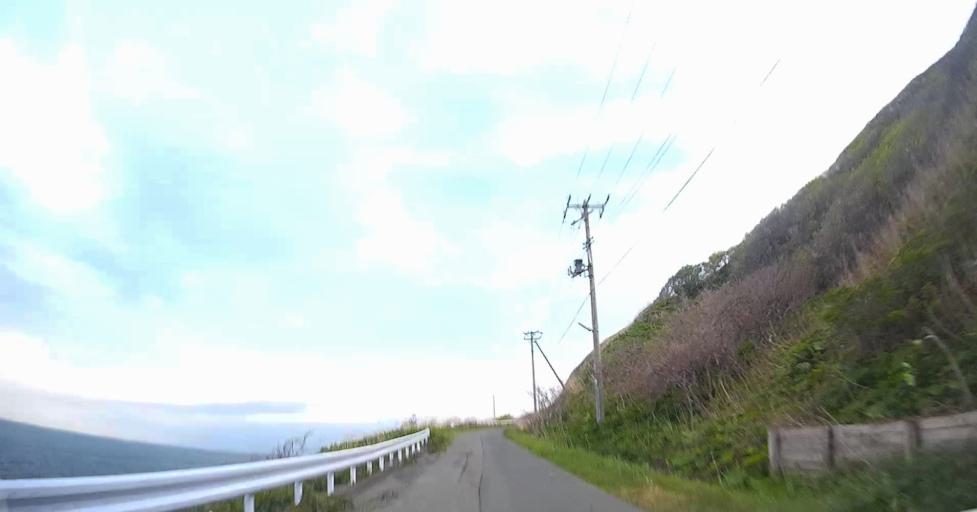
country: JP
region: Aomori
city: Shimokizukuri
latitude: 41.2474
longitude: 140.3436
